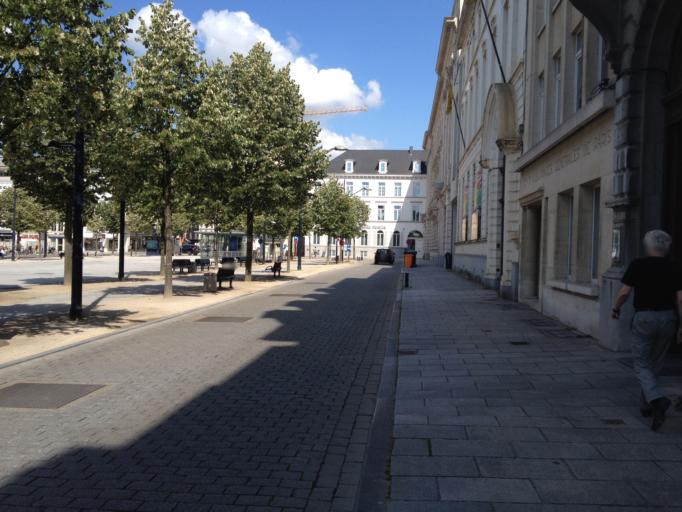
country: BE
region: Flanders
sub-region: Provincie Oost-Vlaanderen
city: Gent
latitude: 51.0499
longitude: 3.7237
